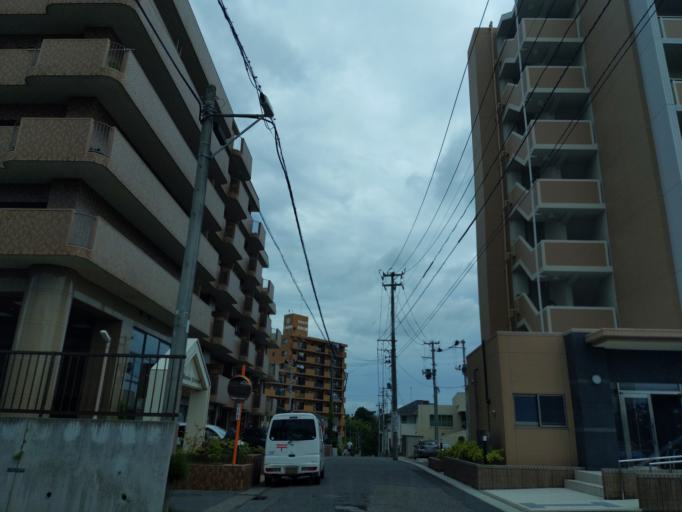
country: JP
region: Fukushima
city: Koriyama
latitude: 37.3889
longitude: 140.3730
